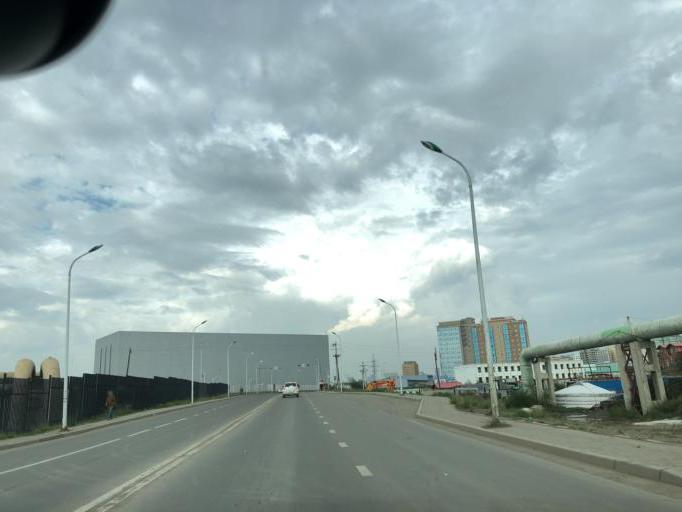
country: MN
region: Ulaanbaatar
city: Ulaanbaatar
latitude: 47.9024
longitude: 106.8703
